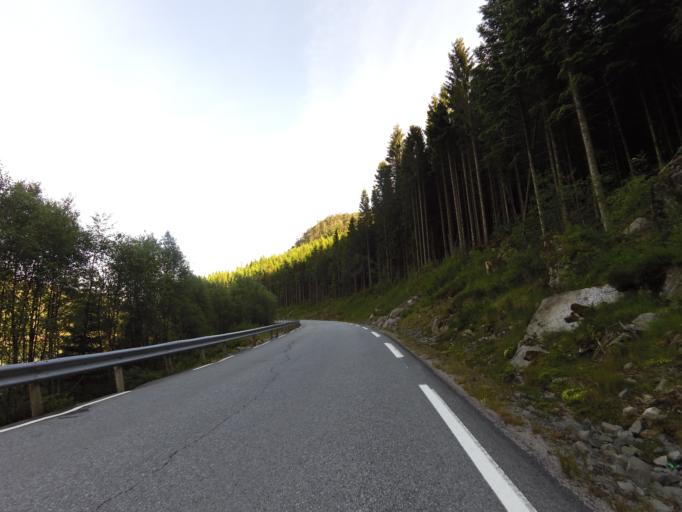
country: NO
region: Vest-Agder
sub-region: Flekkefjord
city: Flekkefjord
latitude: 58.2831
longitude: 6.6188
